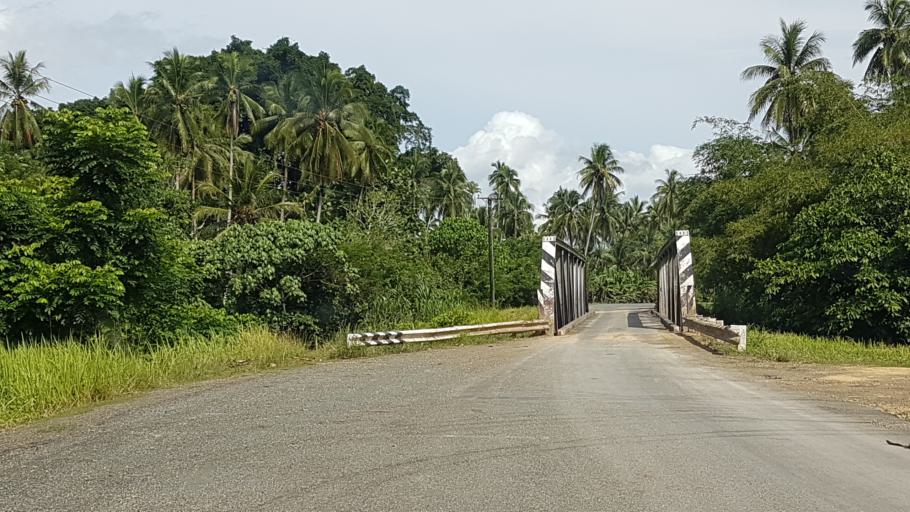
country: PG
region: Madang
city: Madang
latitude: -4.9811
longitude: 145.7769
